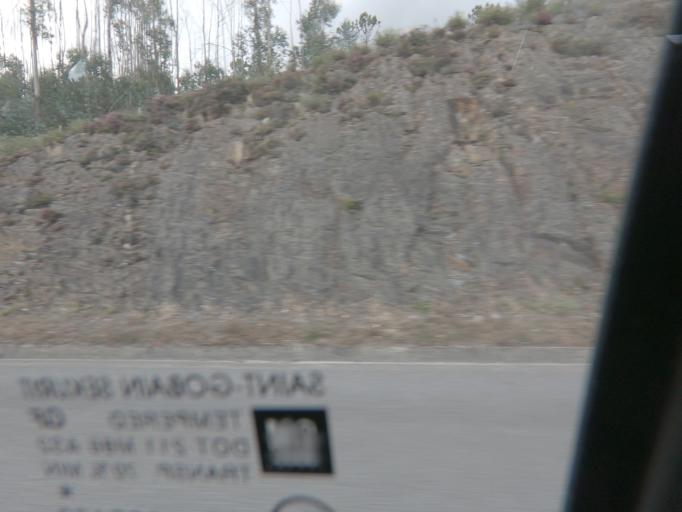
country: PT
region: Porto
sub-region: Paredes
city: Recarei
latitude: 41.1732
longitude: -8.4133
